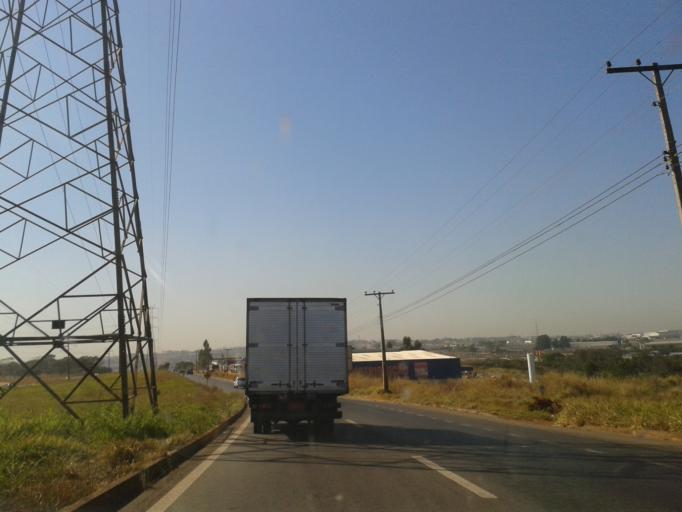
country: BR
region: Goias
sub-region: Aparecida De Goiania
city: Aparecida de Goiania
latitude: -16.7852
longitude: -49.2682
